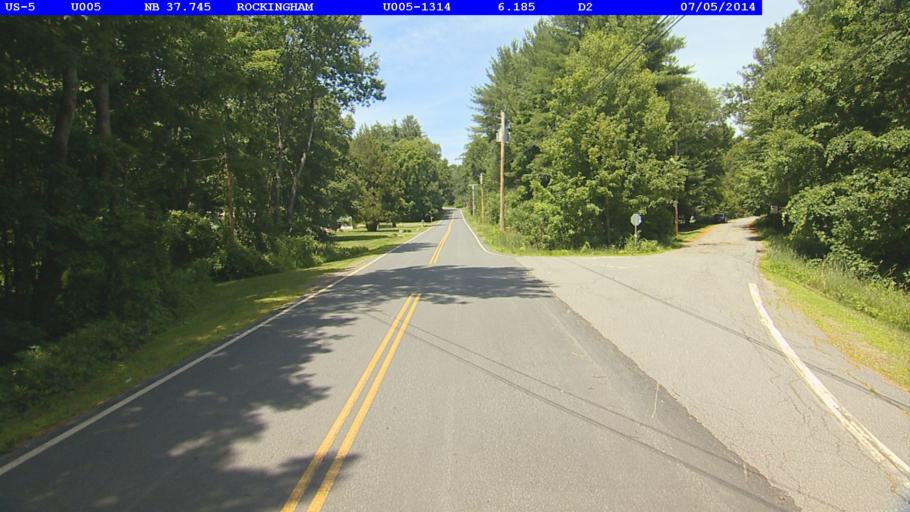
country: US
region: Vermont
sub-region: Windham County
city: Rockingham
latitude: 43.2040
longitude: -72.4502
